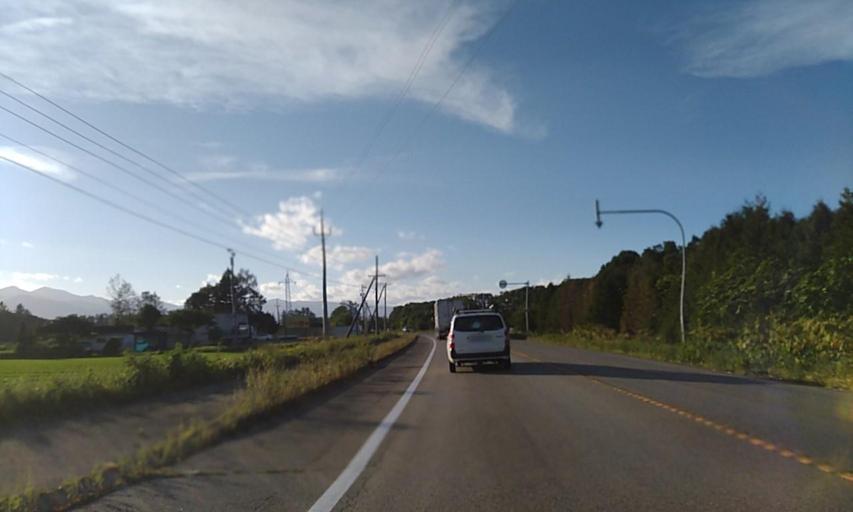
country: JP
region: Hokkaido
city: Obihiro
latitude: 42.9321
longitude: 142.9767
